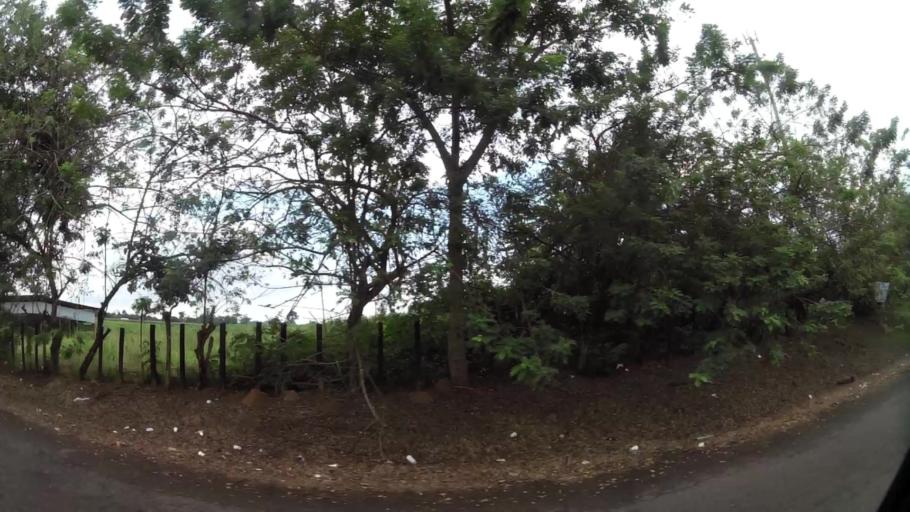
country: PA
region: Panama
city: Cabra Numero Uno
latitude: 9.1133
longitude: -79.3551
